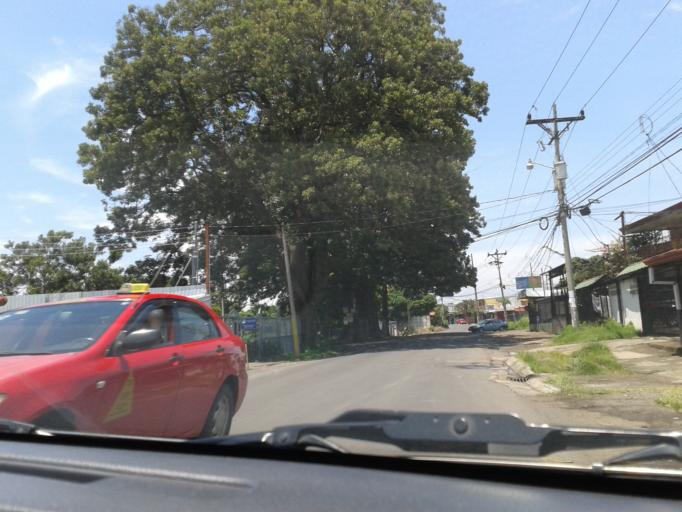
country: CR
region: Alajuela
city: Alajuela
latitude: 10.0059
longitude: -84.2327
